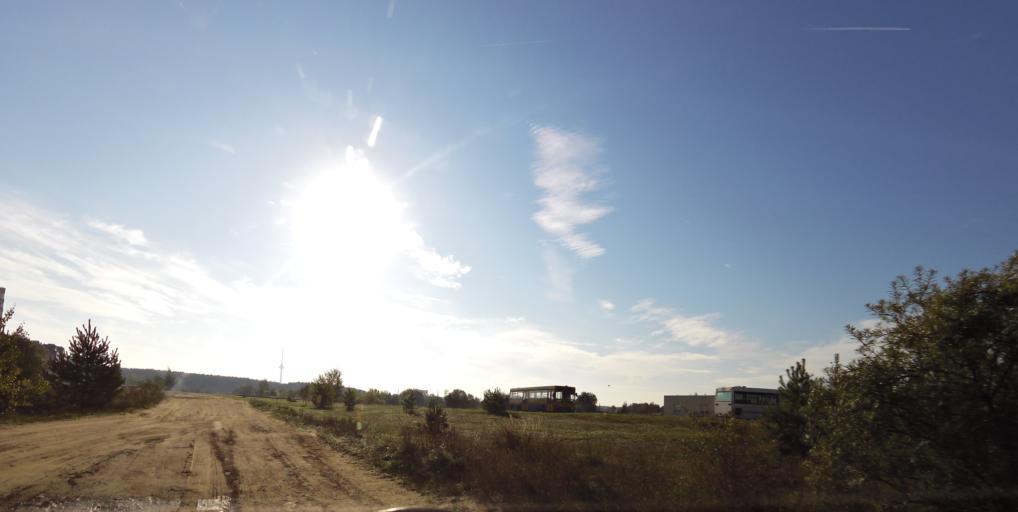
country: LT
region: Vilnius County
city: Pilaite
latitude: 54.7041
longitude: 25.1720
